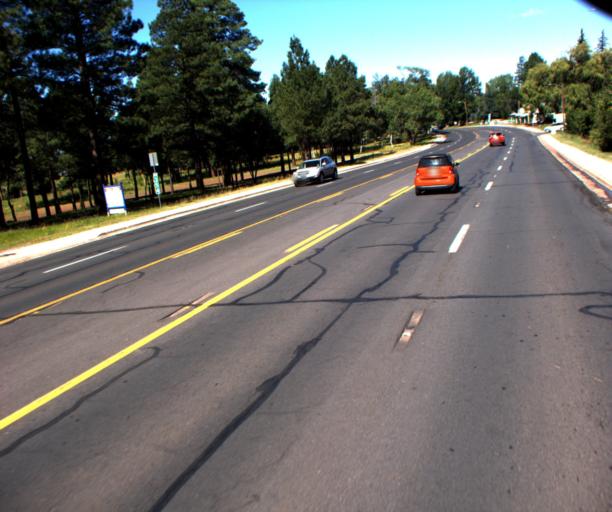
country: US
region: Arizona
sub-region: Navajo County
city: Pinetop-Lakeside
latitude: 34.1253
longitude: -109.9291
